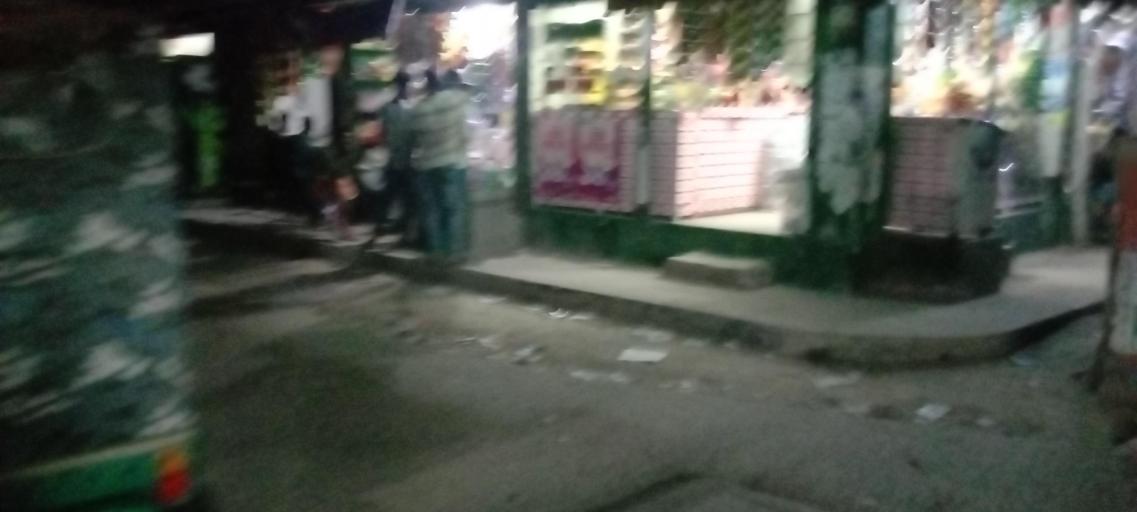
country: BD
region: Dhaka
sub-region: Dhaka
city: Dhaka
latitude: 23.6553
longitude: 90.4473
